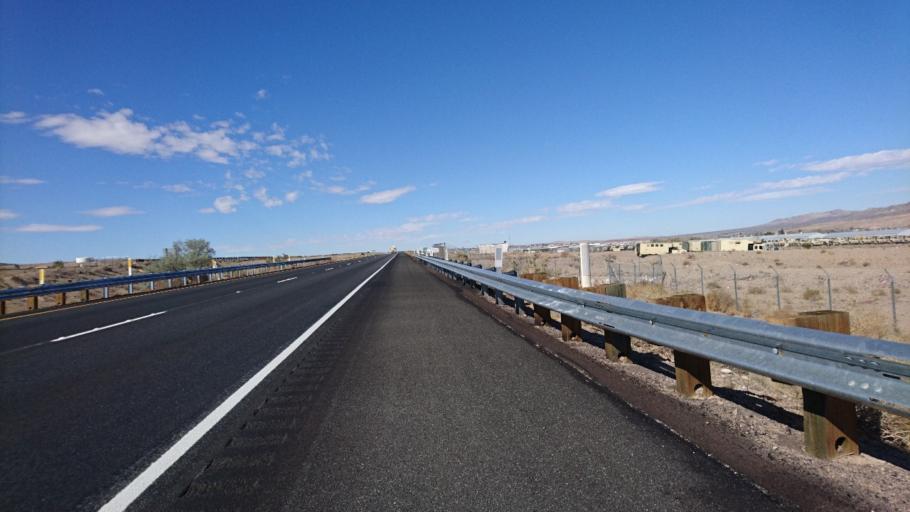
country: US
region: California
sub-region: San Bernardino County
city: Barstow
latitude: 34.8669
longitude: -116.9466
